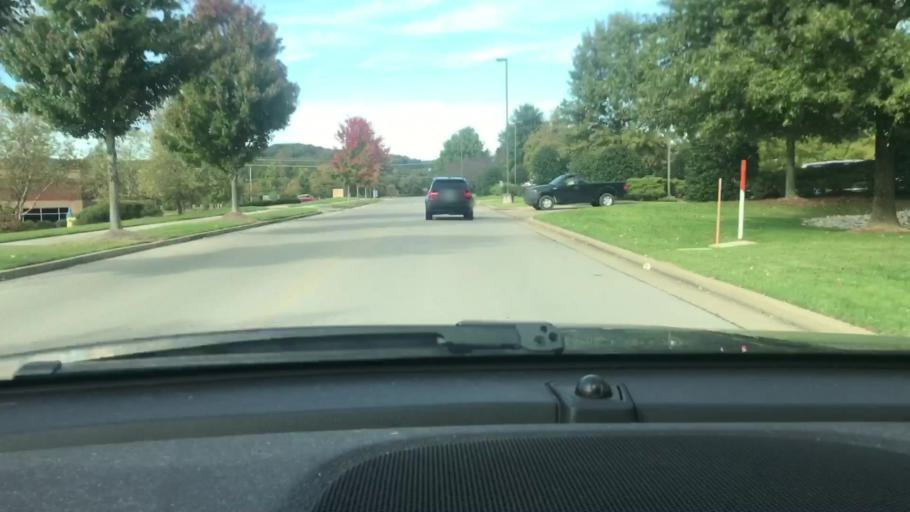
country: US
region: Tennessee
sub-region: Williamson County
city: Franklin
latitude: 35.9505
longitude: -86.8323
